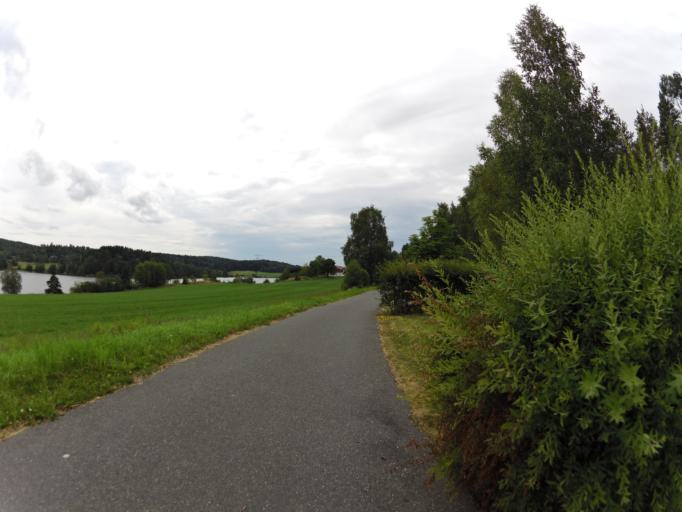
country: NO
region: Akershus
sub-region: As
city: As
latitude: 59.6844
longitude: 10.7415
